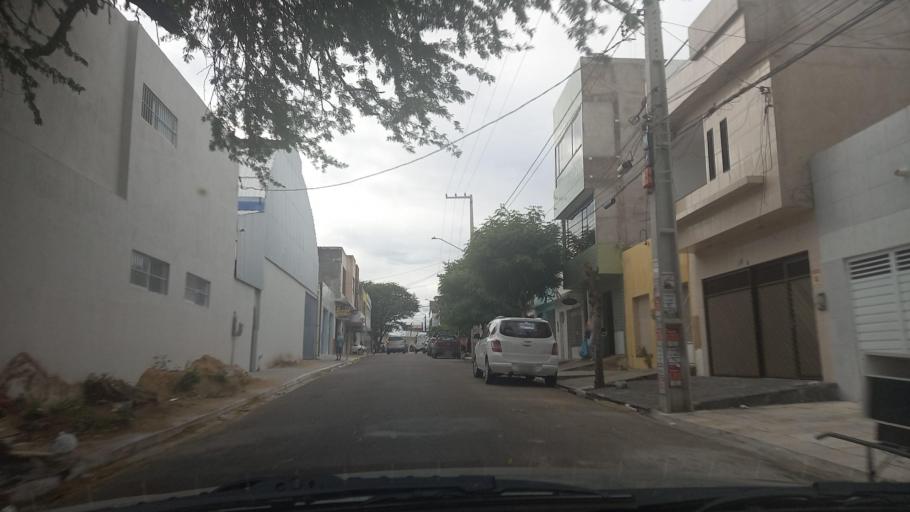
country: BR
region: Pernambuco
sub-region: Caruaru
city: Caruaru
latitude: -8.2769
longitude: -35.9803
